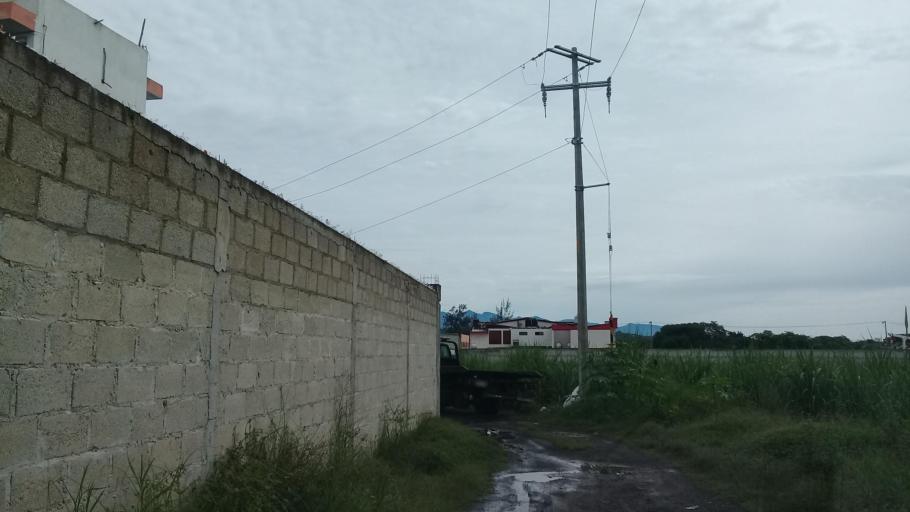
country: MX
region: Veracruz
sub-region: Emiliano Zapata
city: Dos Rios
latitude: 19.4840
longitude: -96.8056
